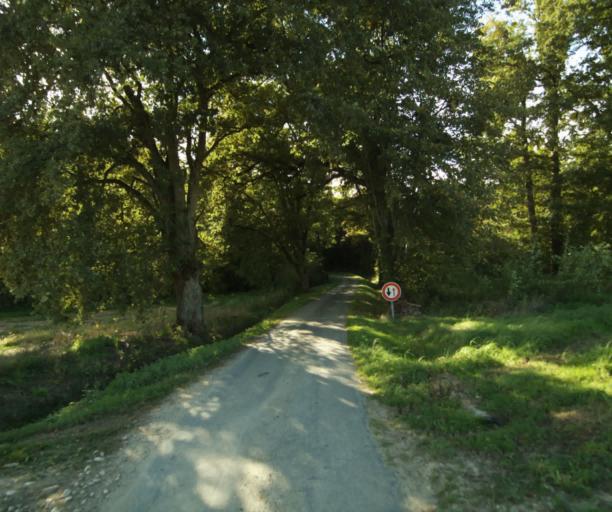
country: FR
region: Midi-Pyrenees
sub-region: Departement du Gers
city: Eauze
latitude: 43.8621
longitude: 0.0392
